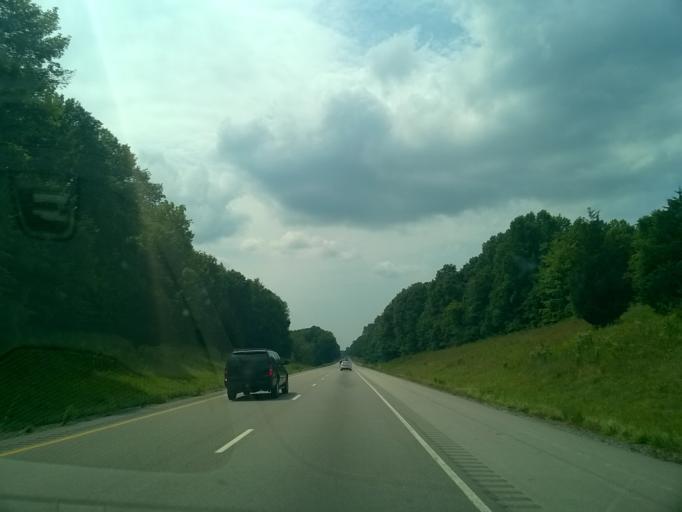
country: US
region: Indiana
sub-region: Putnam County
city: Cloverdale
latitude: 39.5227
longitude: -86.8942
